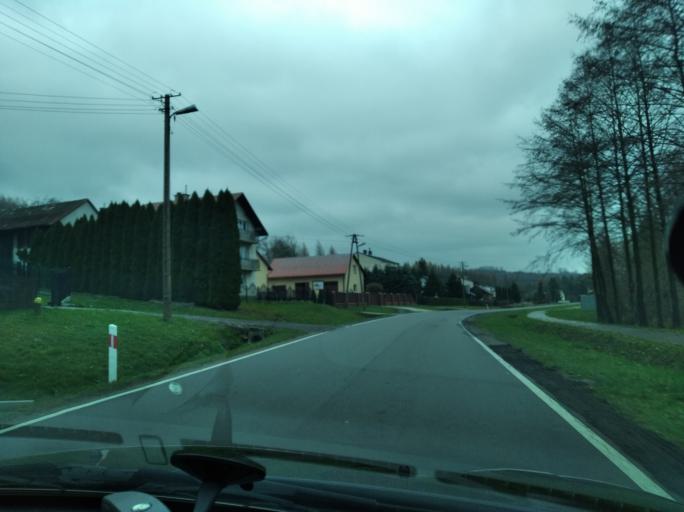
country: PL
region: Subcarpathian Voivodeship
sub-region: Powiat przeworski
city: Manasterz
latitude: 49.9309
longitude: 22.3398
